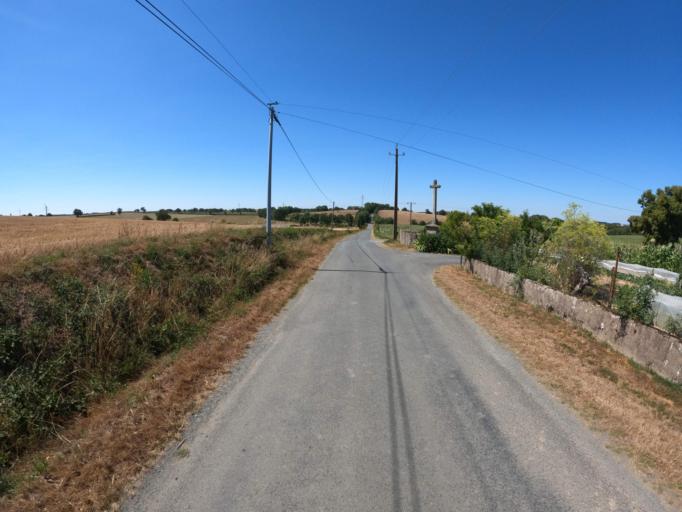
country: FR
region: Pays de la Loire
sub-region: Departement de Maine-et-Loire
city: Saint-Christophe-du-Bois
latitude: 47.0358
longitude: -0.9494
